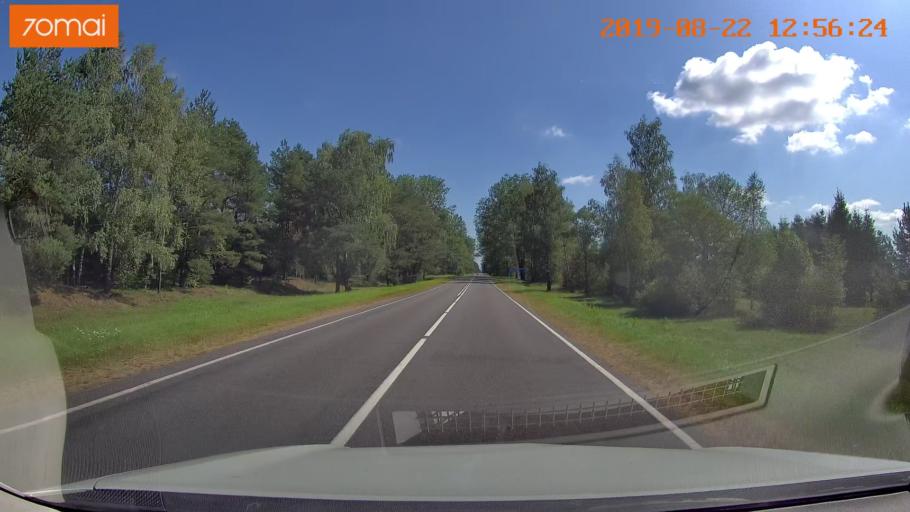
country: BY
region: Minsk
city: Prawdzinski
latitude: 53.4331
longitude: 27.7304
